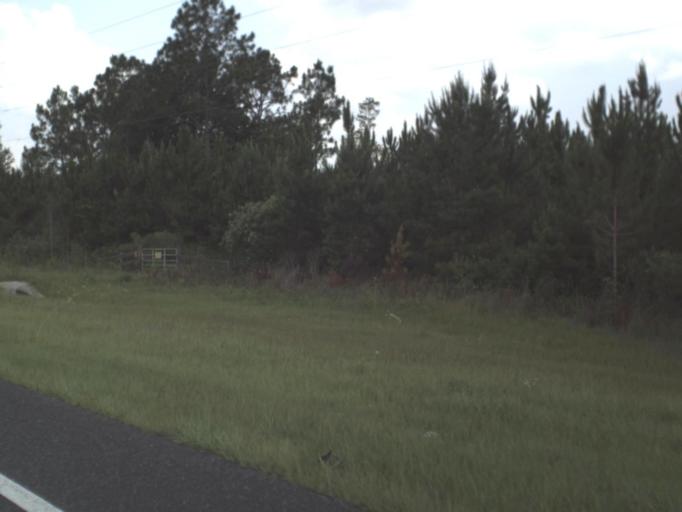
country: US
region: Florida
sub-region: Levy County
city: Bronson
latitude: 29.4769
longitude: -82.6882
